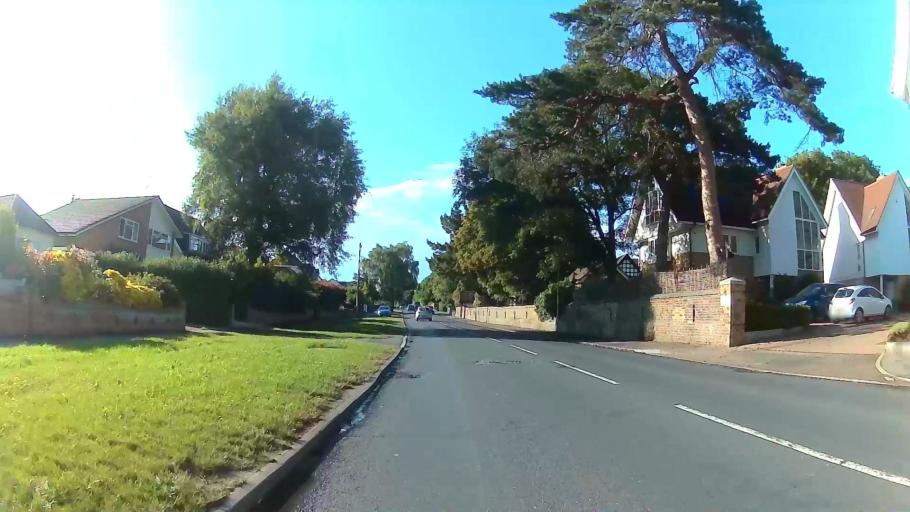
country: GB
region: England
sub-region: Essex
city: Writtle
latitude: 51.7449
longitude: 0.4441
